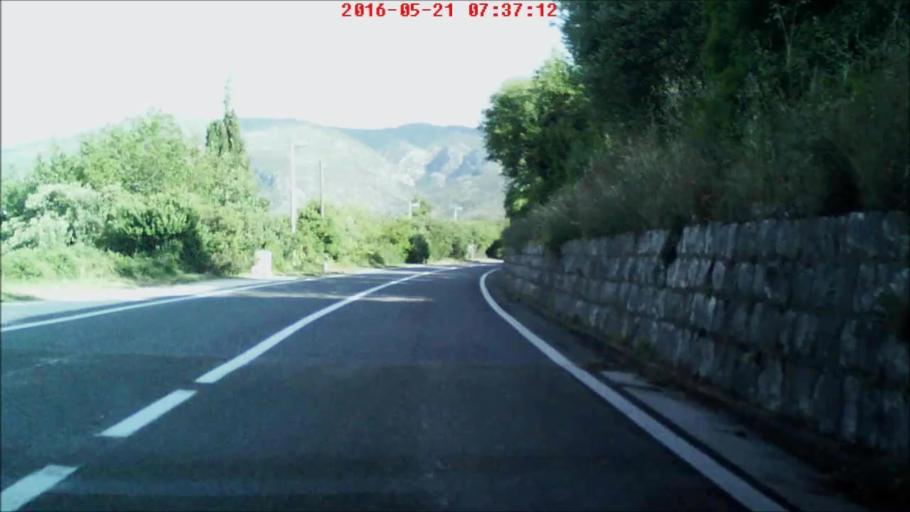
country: HR
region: Dubrovacko-Neretvanska
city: Podgora
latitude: 42.7878
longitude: 17.8557
